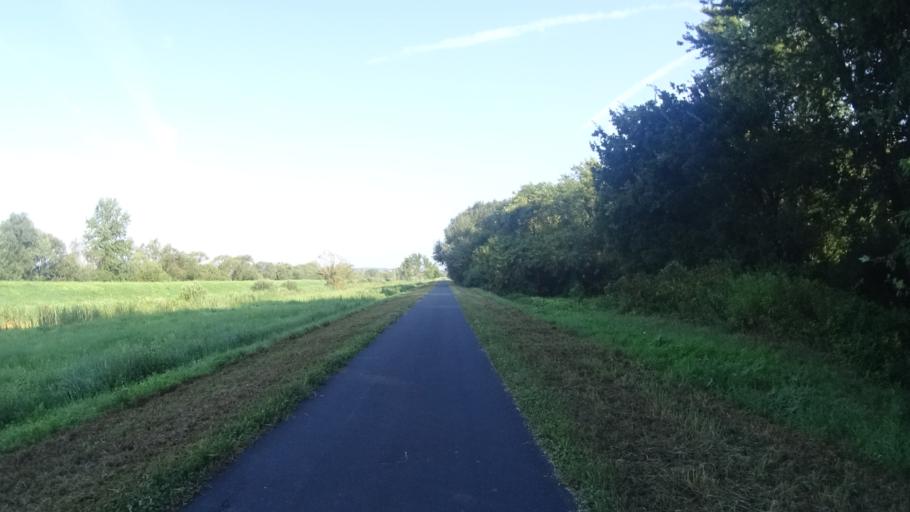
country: HU
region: Zala
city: Sarmellek
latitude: 46.6485
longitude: 17.1515
